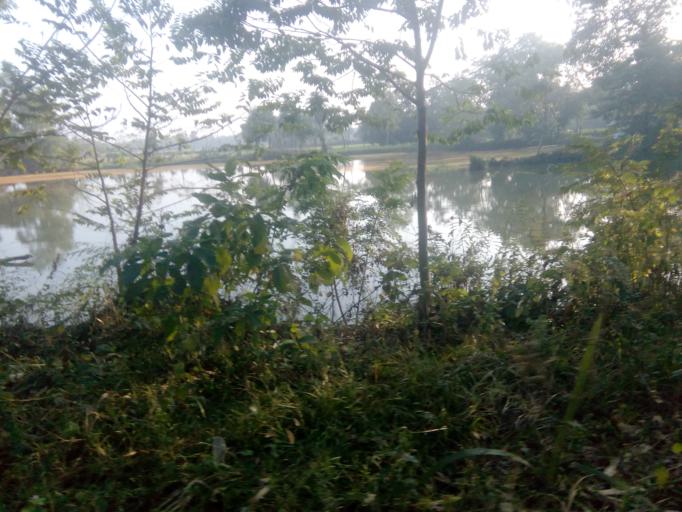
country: IN
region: Tripura
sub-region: West Tripura
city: Sonamura
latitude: 23.4146
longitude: 91.2408
